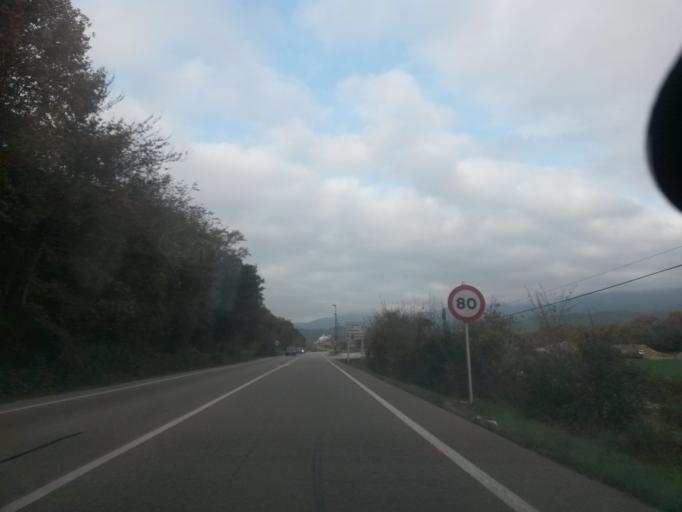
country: ES
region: Catalonia
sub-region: Provincia de Girona
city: Besalu
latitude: 42.1889
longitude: 2.7337
